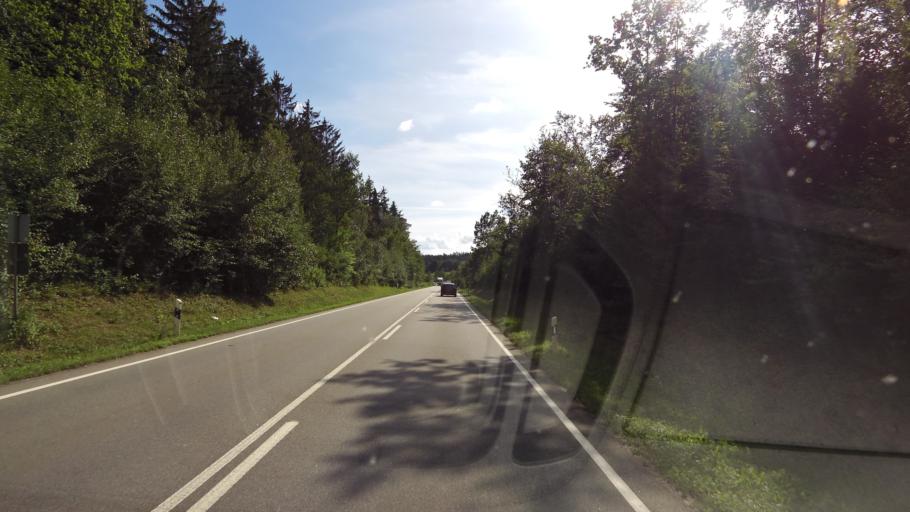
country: DE
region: Bavaria
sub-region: Lower Bavaria
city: Ascha
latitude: 49.0042
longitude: 12.6335
